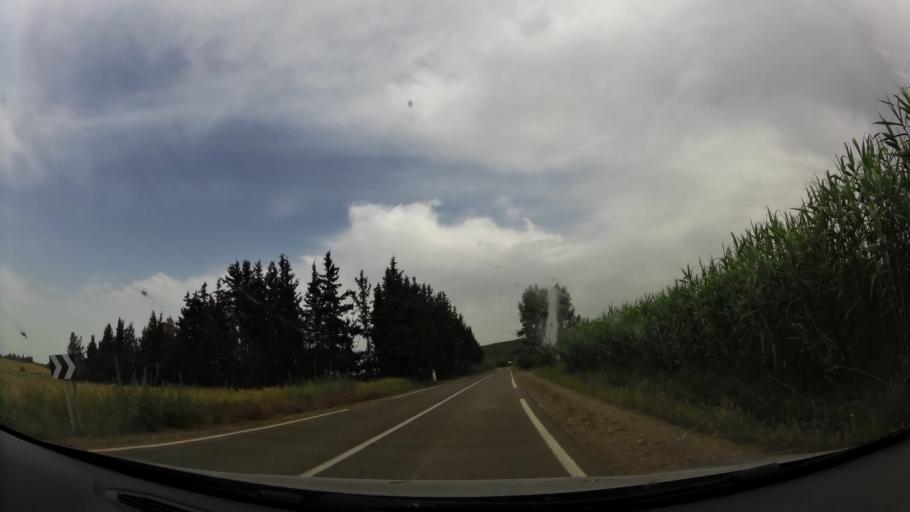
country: MA
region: Rabat-Sale-Zemmour-Zaer
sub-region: Khemisset
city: Khemisset
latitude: 33.7552
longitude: -6.2003
